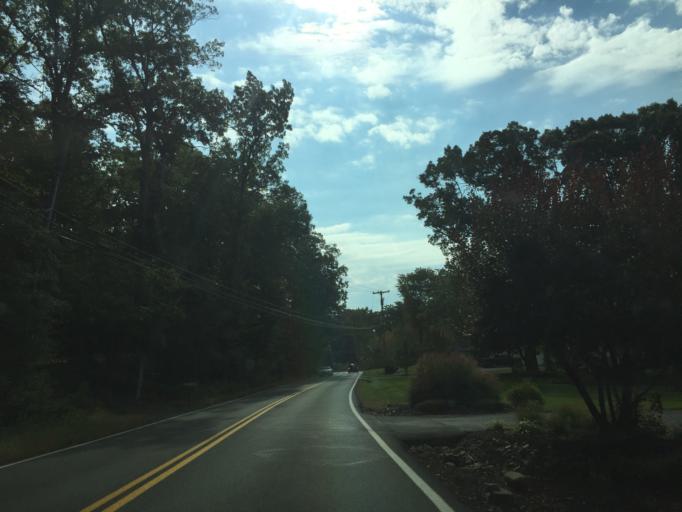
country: US
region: Maryland
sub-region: Harford County
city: Bel Air South
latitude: 39.4777
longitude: -76.2971
